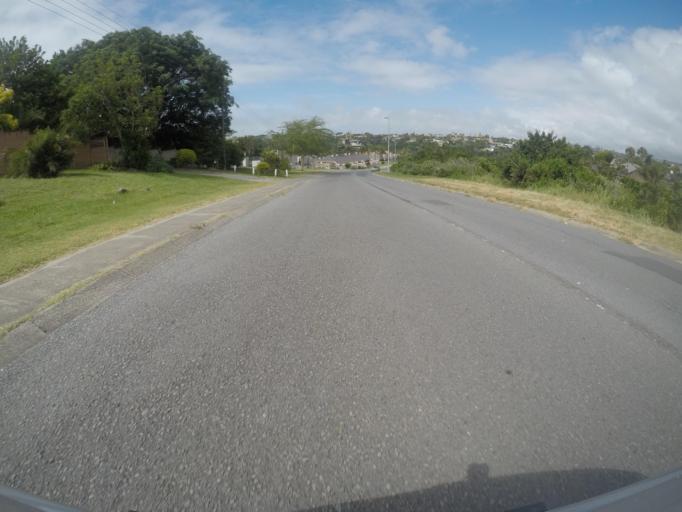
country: ZA
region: Eastern Cape
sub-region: Buffalo City Metropolitan Municipality
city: East London
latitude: -32.9794
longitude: 27.9394
